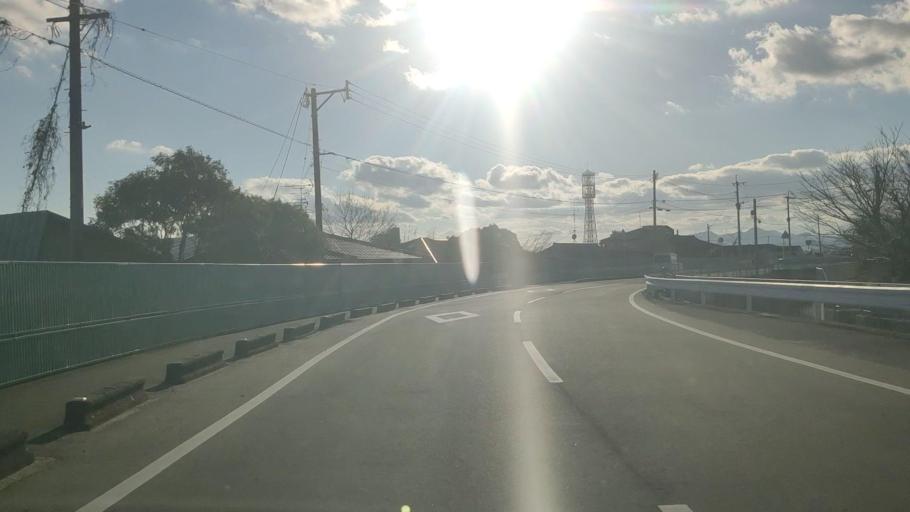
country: JP
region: Saga Prefecture
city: Saga-shi
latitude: 33.3055
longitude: 130.2582
